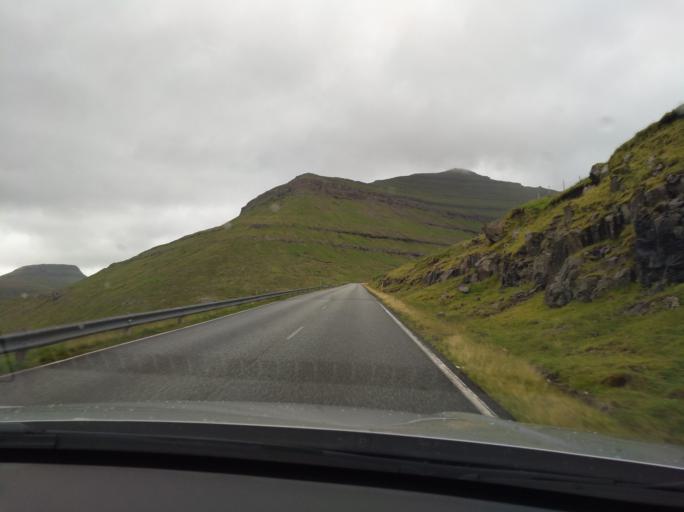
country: FO
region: Eysturoy
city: Fuglafjordur
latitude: 62.2216
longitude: -6.8738
